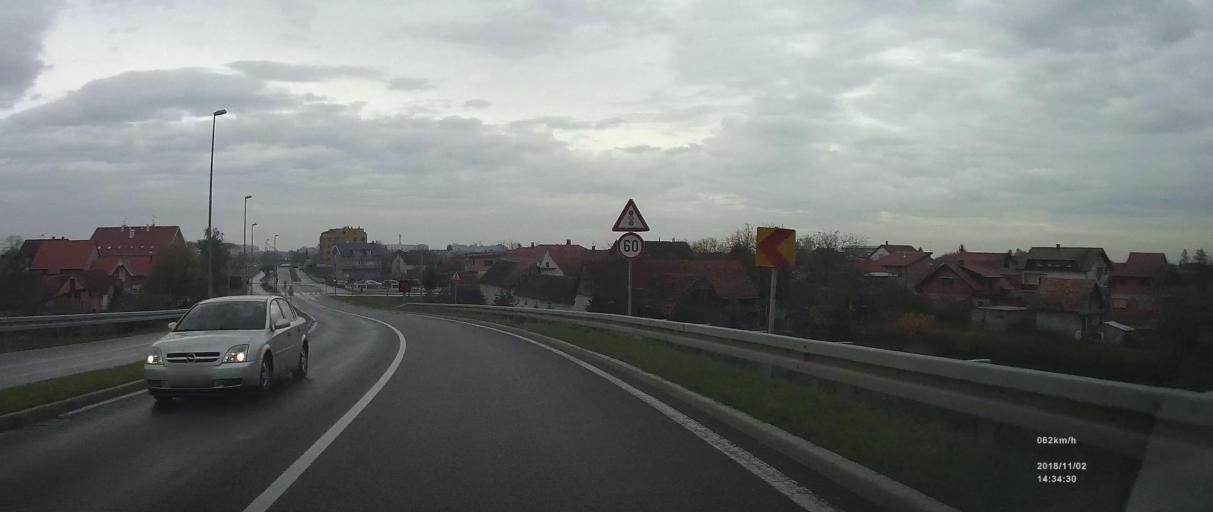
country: HR
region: Zagrebacka
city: Gradici
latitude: 45.6991
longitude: 16.0619
